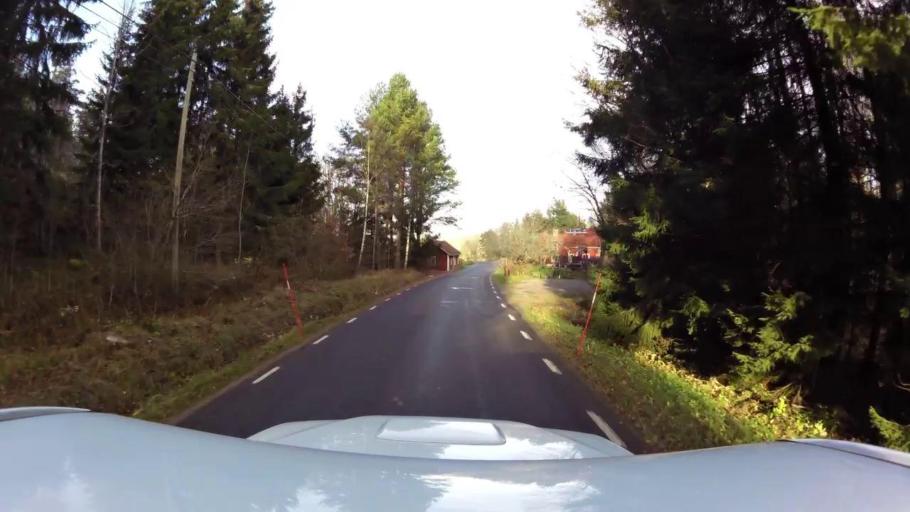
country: SE
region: OEstergoetland
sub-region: Linkopings Kommun
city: Sturefors
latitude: 58.3355
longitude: 15.6527
